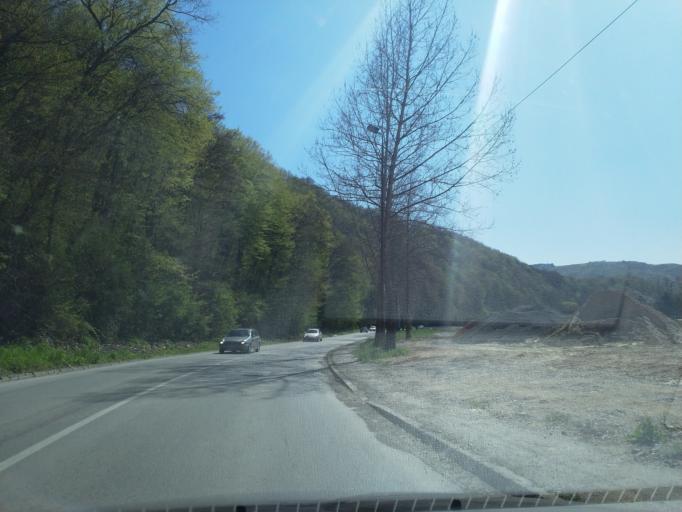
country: RS
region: Central Serbia
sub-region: Kolubarski Okrug
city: Valjevo
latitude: 44.2633
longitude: 19.8780
